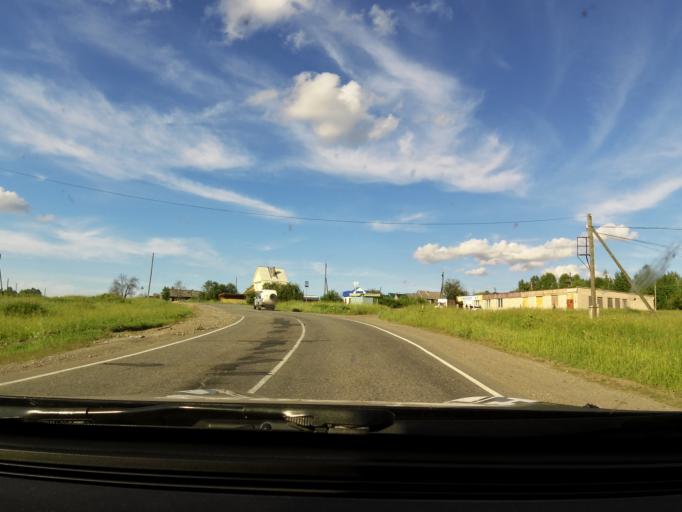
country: RU
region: Kirov
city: Belorechensk
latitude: 58.7134
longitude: 52.3271
